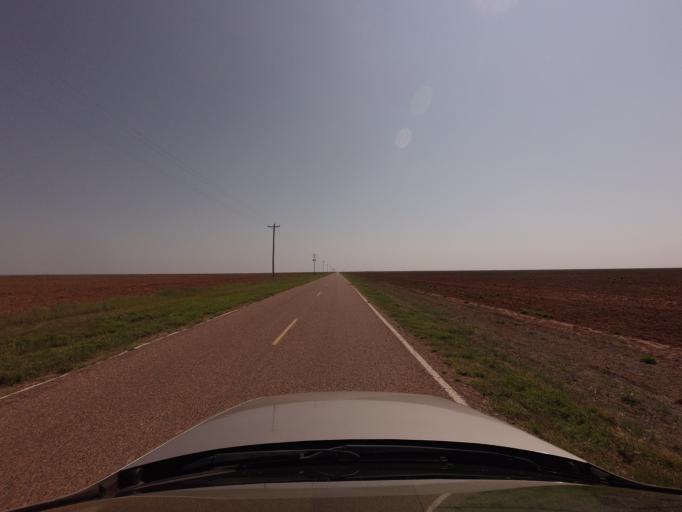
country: US
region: New Mexico
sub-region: Curry County
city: Cannon Air Force Base
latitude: 34.6327
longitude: -103.3153
